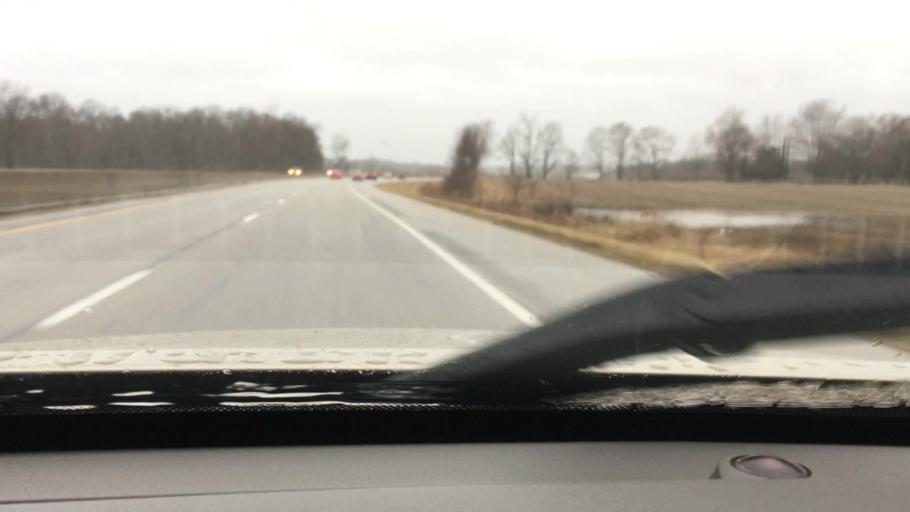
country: US
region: Indiana
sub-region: Delaware County
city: Yorktown
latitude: 40.2165
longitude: -85.5443
